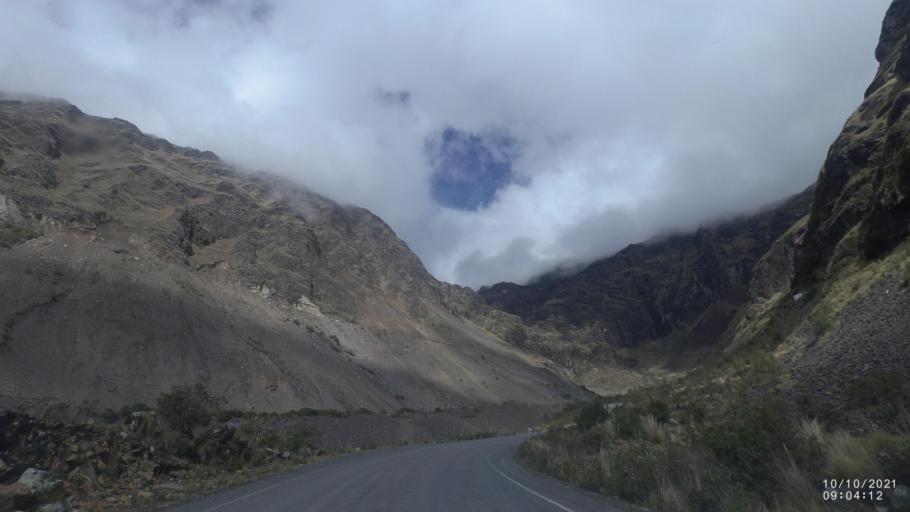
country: BO
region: La Paz
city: Quime
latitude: -17.0021
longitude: -67.2756
